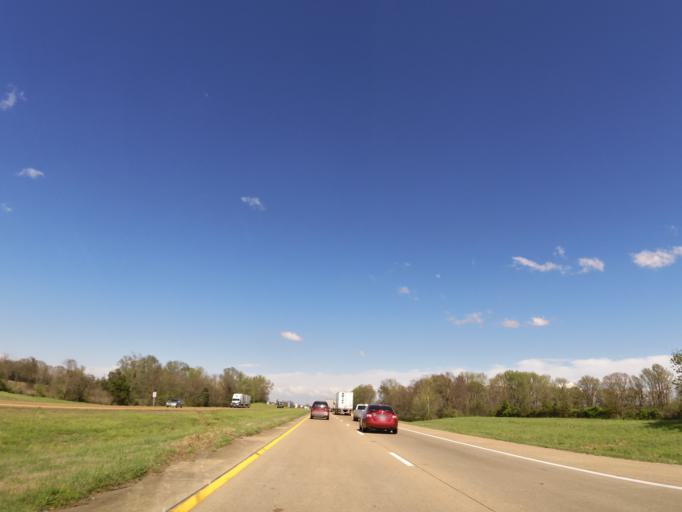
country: US
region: Tennessee
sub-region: Gibson County
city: Medina
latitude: 35.7142
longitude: -88.6466
